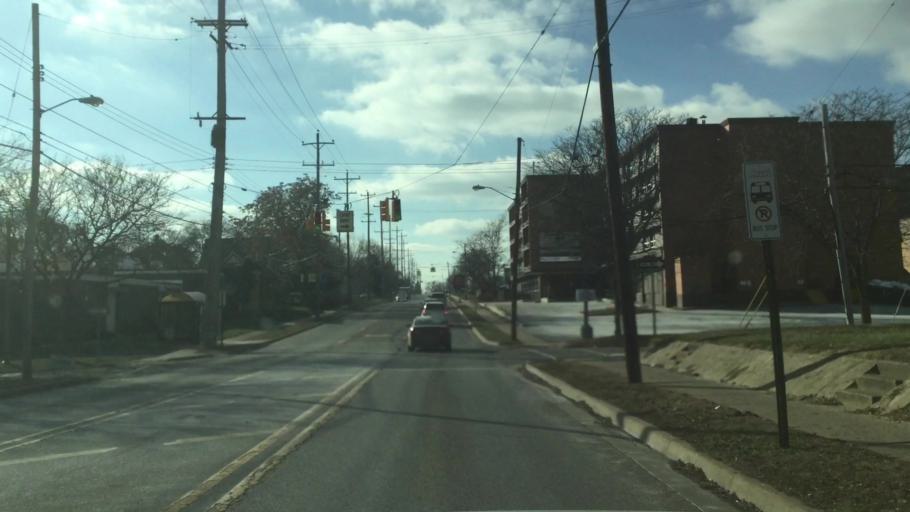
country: US
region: Michigan
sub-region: Genesee County
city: Flint
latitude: 43.0217
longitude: -83.6996
